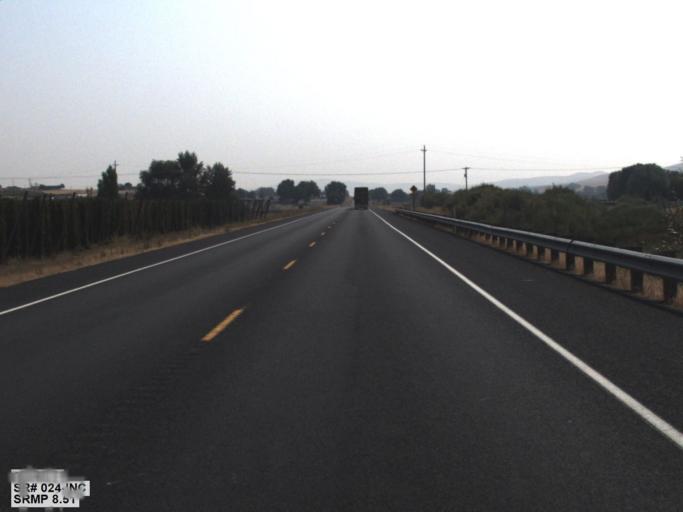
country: US
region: Washington
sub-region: Yakima County
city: Terrace Heights
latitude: 46.5428
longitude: -120.3166
